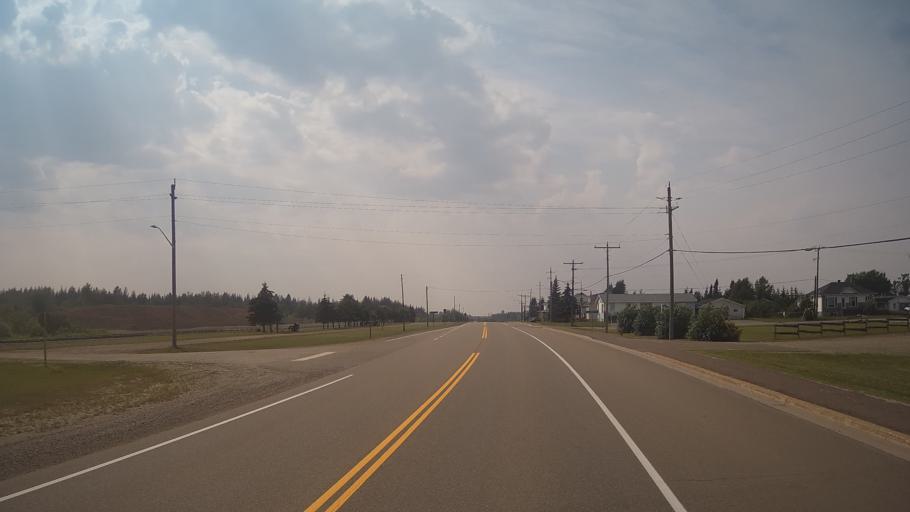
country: CA
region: Ontario
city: Kapuskasing
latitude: 49.4436
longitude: -82.5397
